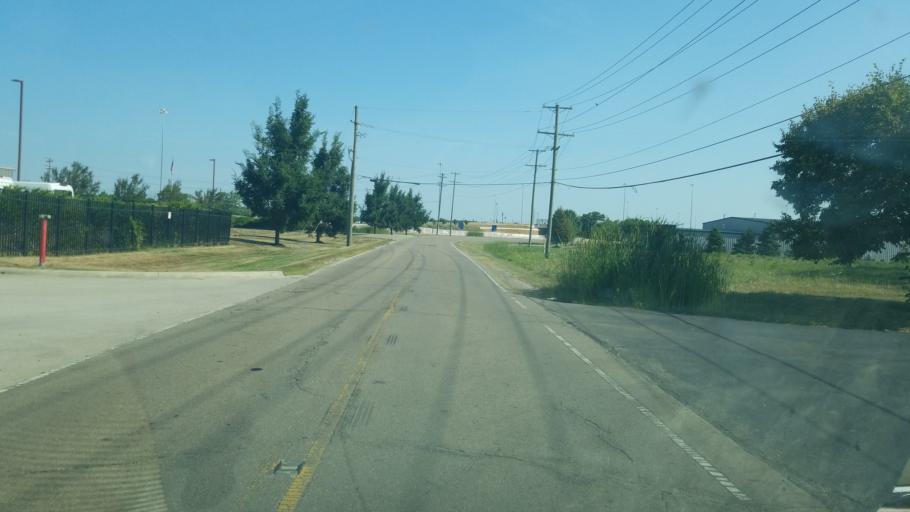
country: US
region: Ohio
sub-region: Franklin County
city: Grove City
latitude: 39.8361
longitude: -83.0919
